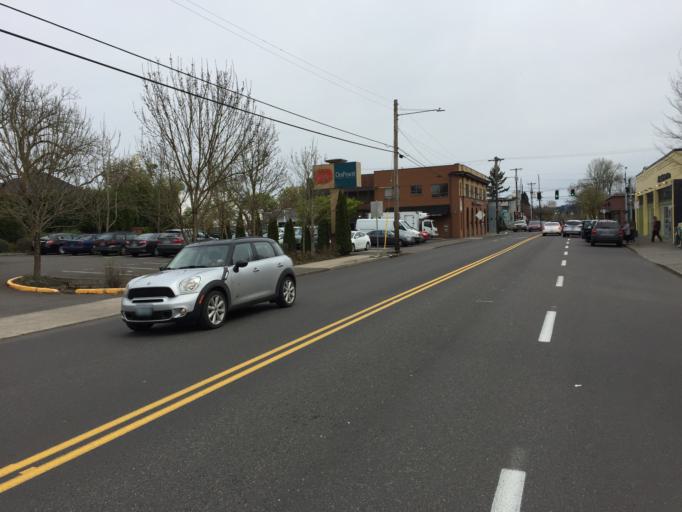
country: US
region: Oregon
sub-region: Clackamas County
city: Milwaukie
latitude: 45.4643
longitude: -122.6544
